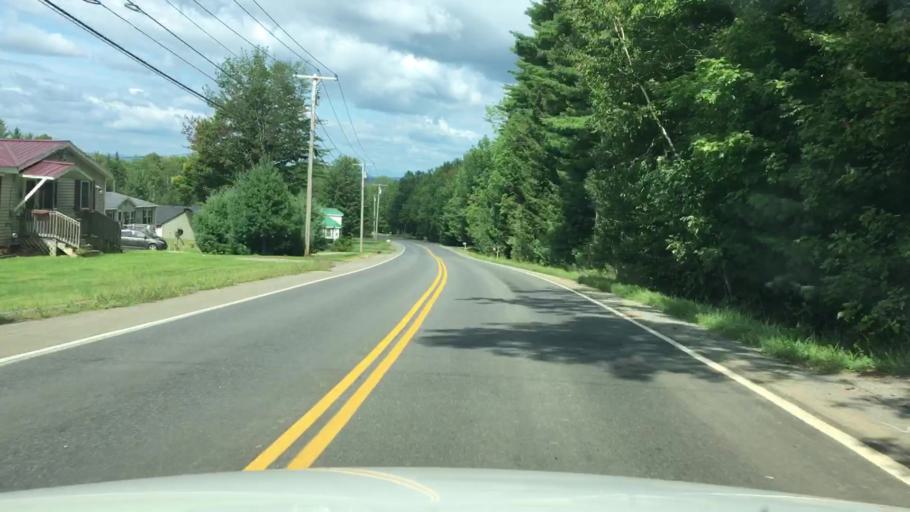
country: US
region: Maine
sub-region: Somerset County
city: Skowhegan
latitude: 44.7456
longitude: -69.6941
